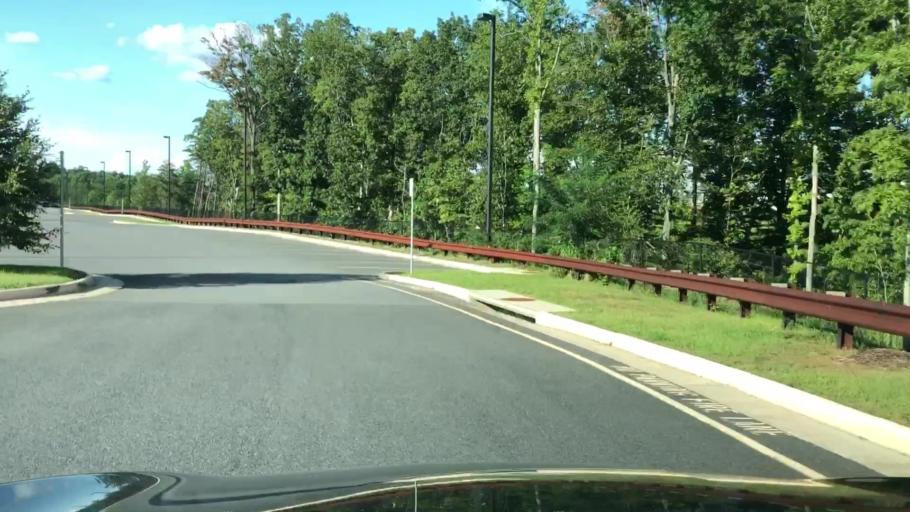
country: US
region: Virginia
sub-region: Stafford County
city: Stafford
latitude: 38.4300
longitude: -77.4342
